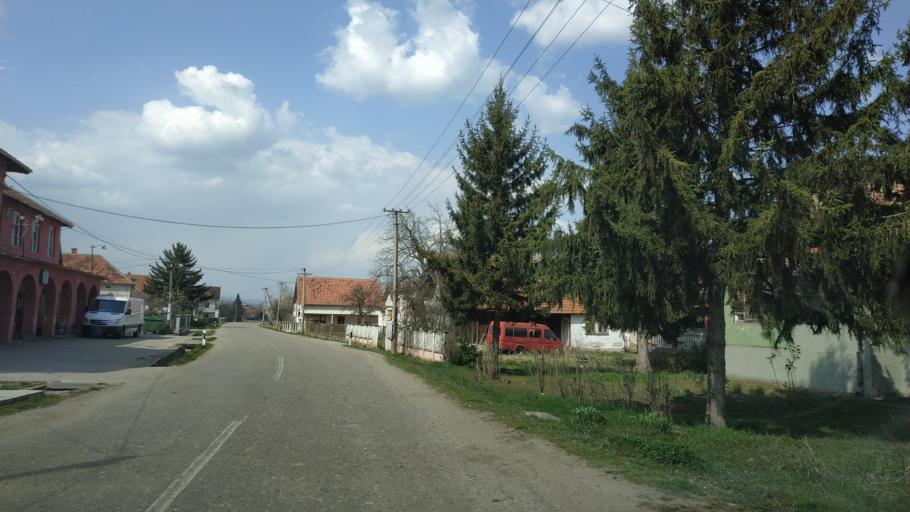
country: RS
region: Central Serbia
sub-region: Nisavski Okrug
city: Razanj
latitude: 43.5795
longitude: 21.5743
